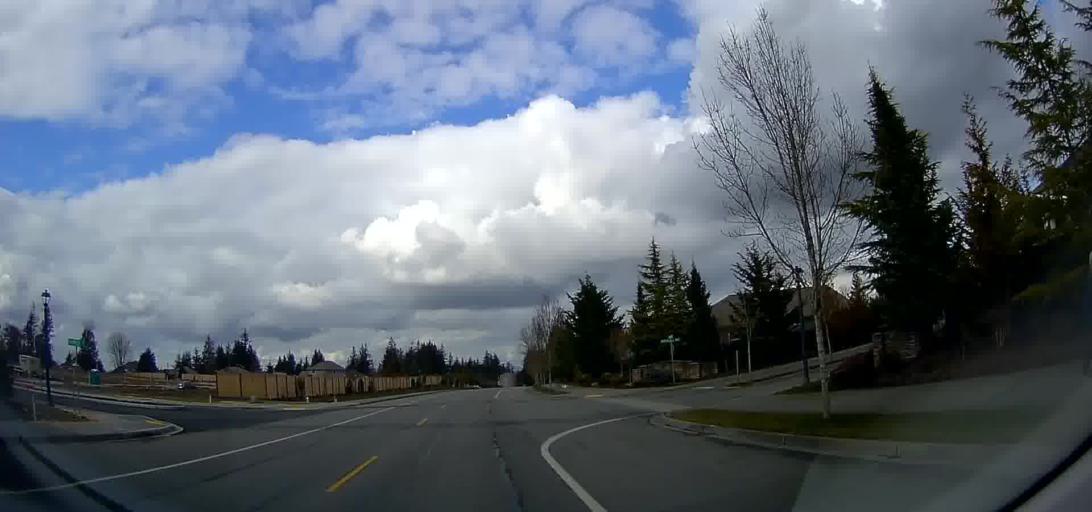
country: US
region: Washington
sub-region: Skagit County
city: Big Lake
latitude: 48.4151
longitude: -122.2869
